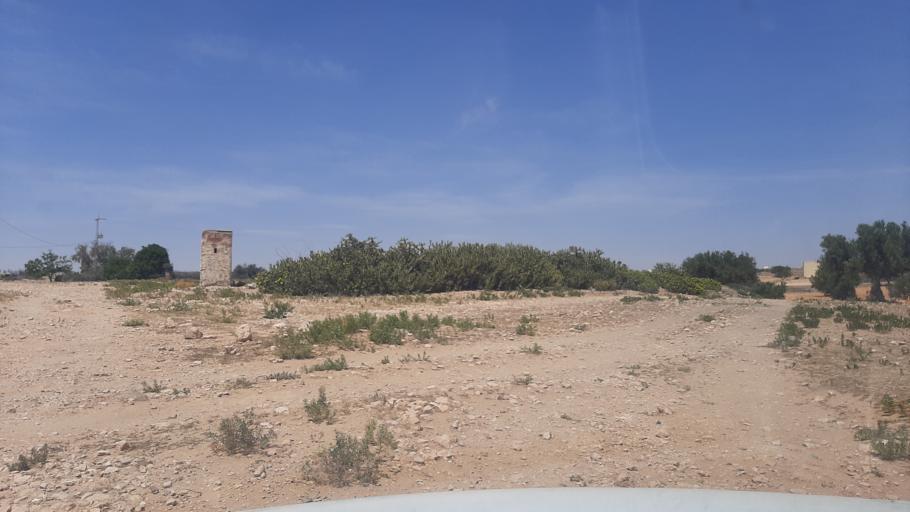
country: TN
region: Safaqis
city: Bi'r `Ali Bin Khalifah
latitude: 34.5656
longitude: 10.3453
